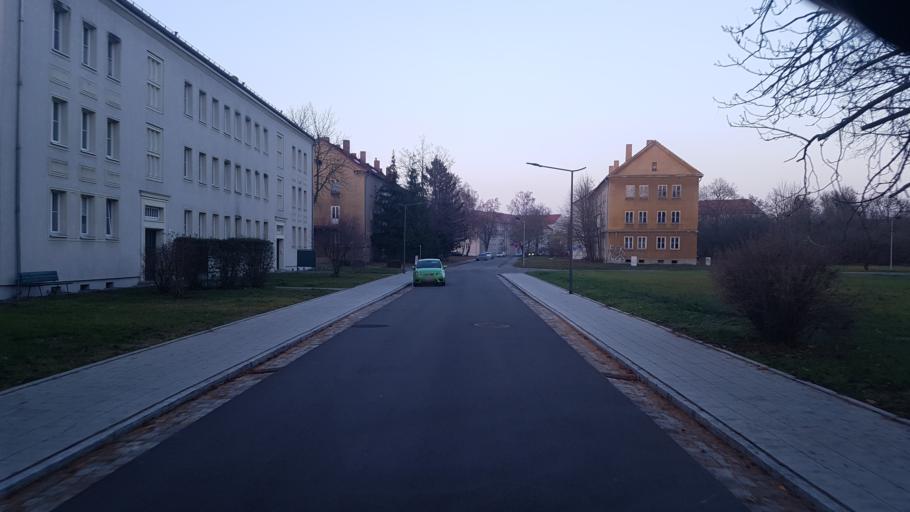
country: DE
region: Brandenburg
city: Lauchhammer
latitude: 51.4962
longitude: 13.7476
